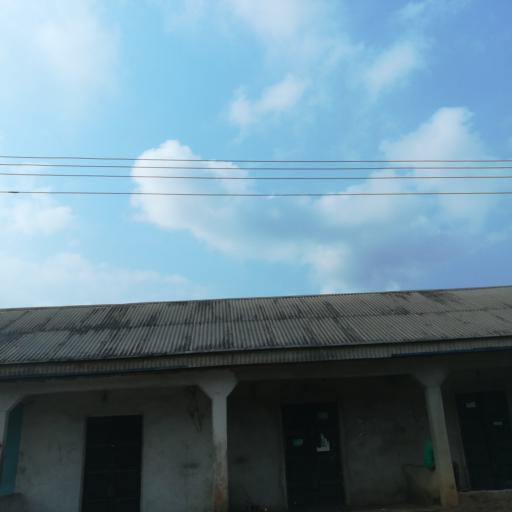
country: NG
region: Rivers
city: Okrika
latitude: 4.7747
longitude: 7.1588
